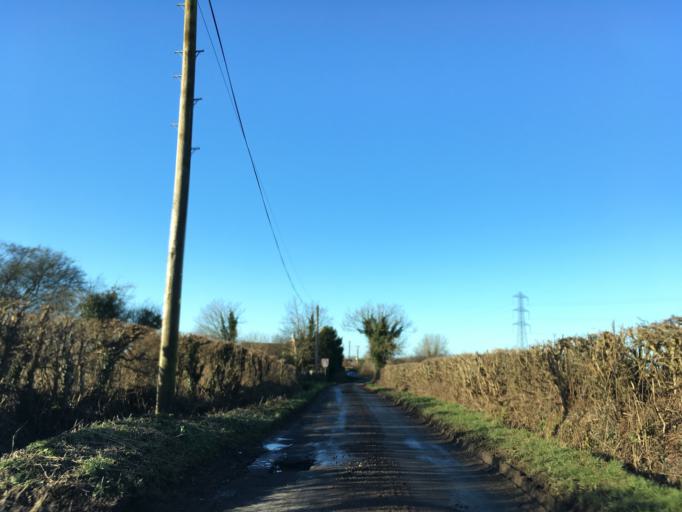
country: GB
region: England
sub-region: South Gloucestershire
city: Horton
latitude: 51.5498
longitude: -2.3539
